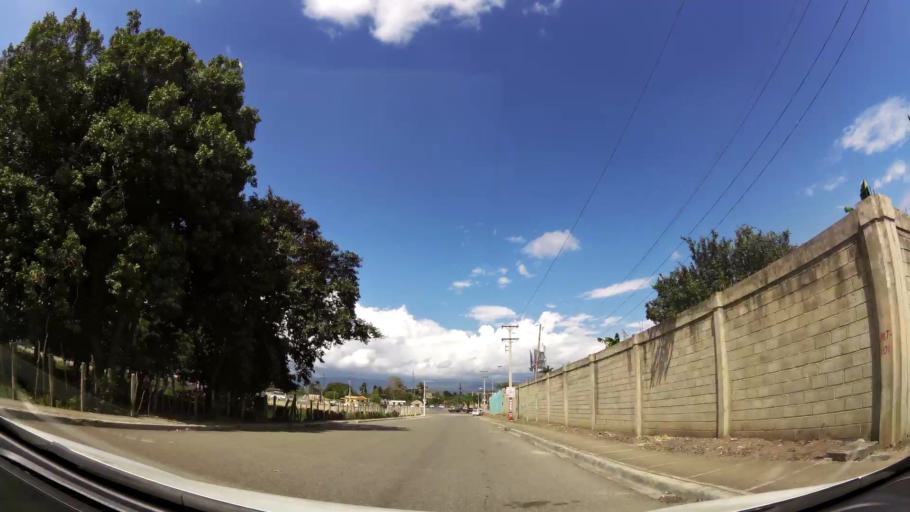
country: DO
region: Santiago
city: Licey al Medio
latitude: 19.3817
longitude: -70.6136
